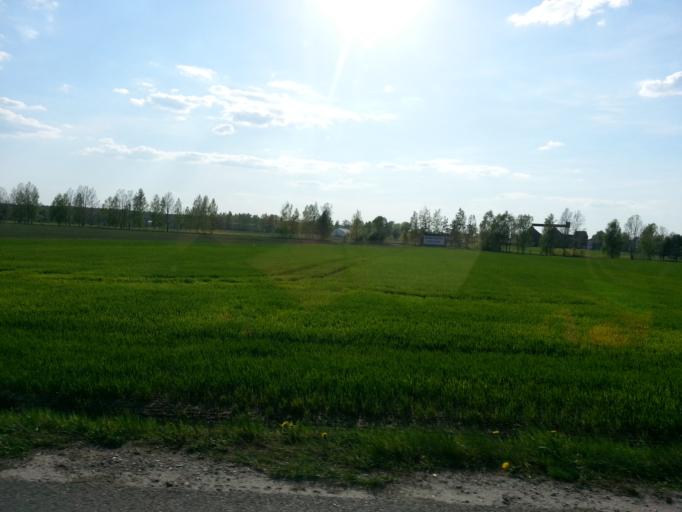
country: LT
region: Panevezys
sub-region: Panevezys City
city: Panevezys
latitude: 55.8547
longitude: 24.3501
